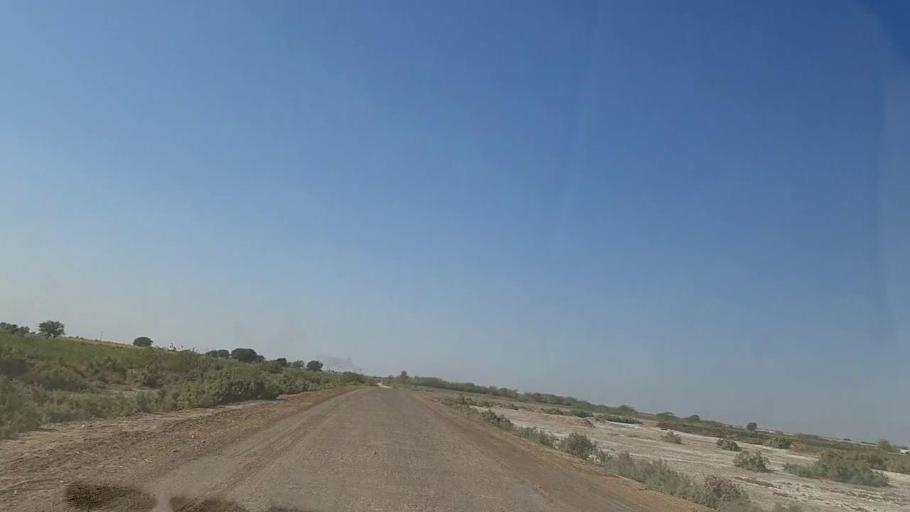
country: PK
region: Sindh
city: Digri
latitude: 25.1429
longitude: 69.0141
